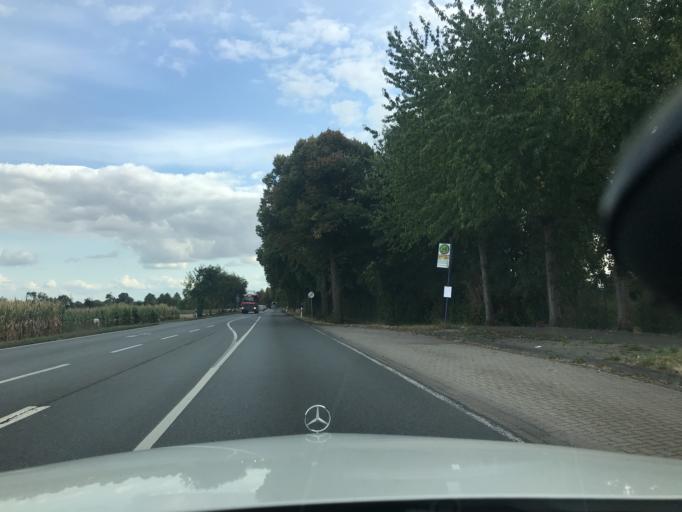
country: DE
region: North Rhine-Westphalia
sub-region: Regierungsbezirk Arnsberg
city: Lippstadt
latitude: 51.6542
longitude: 8.3679
